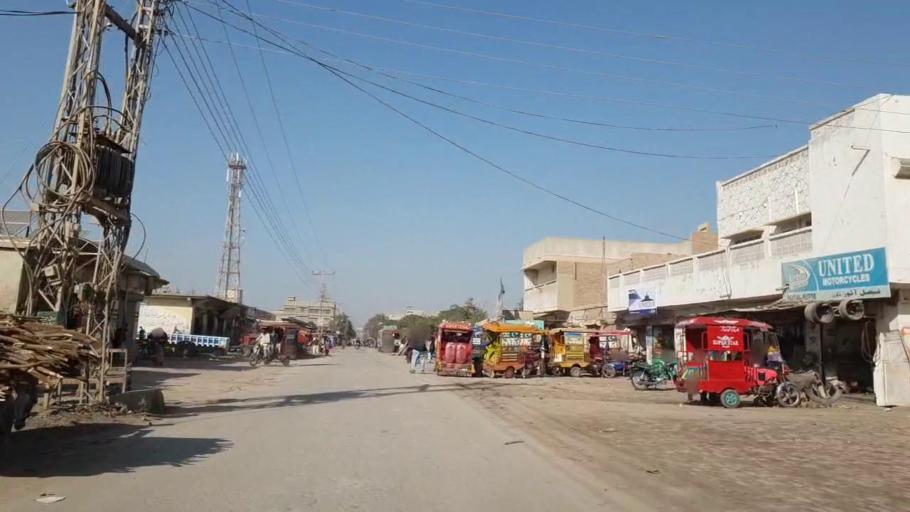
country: PK
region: Sindh
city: Digri
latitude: 25.1507
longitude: 69.1116
